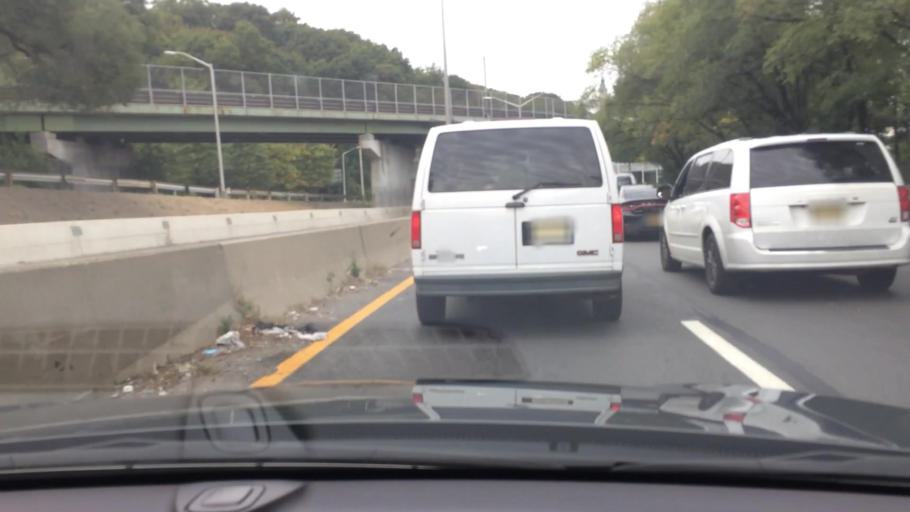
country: US
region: New York
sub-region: New York County
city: Inwood
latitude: 40.8349
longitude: -73.9352
